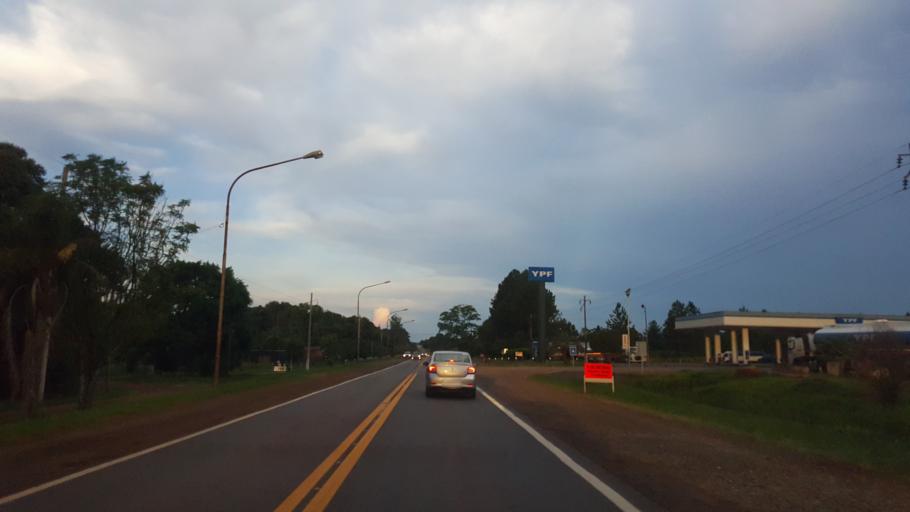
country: AR
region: Misiones
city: Jardin America
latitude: -27.0296
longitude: -55.2162
